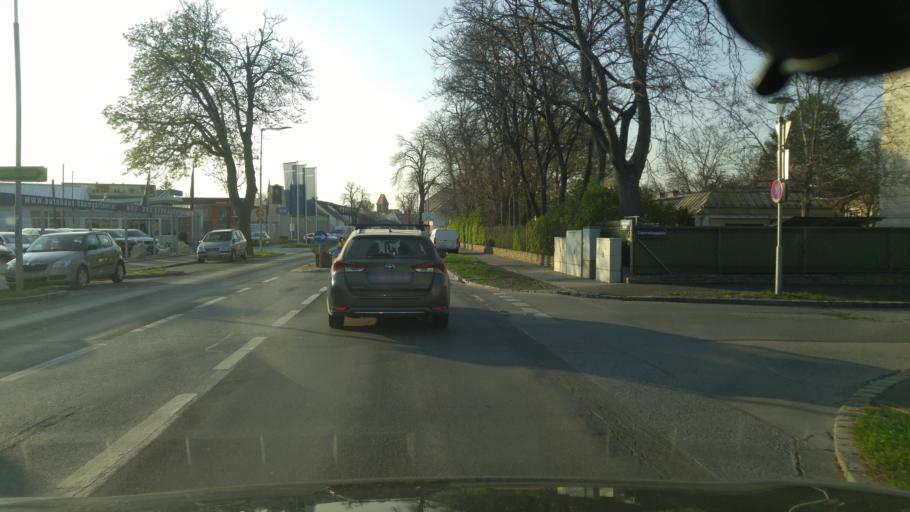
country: AT
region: Lower Austria
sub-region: Politischer Bezirk Wien-Umgebung
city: Himberg
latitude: 48.0780
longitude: 16.4435
